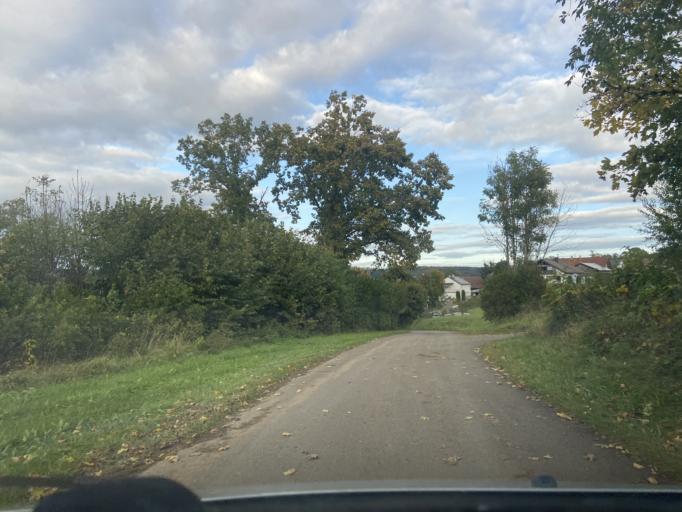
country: DE
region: Baden-Wuerttemberg
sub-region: Tuebingen Region
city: Bingen
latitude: 48.1067
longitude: 9.2701
